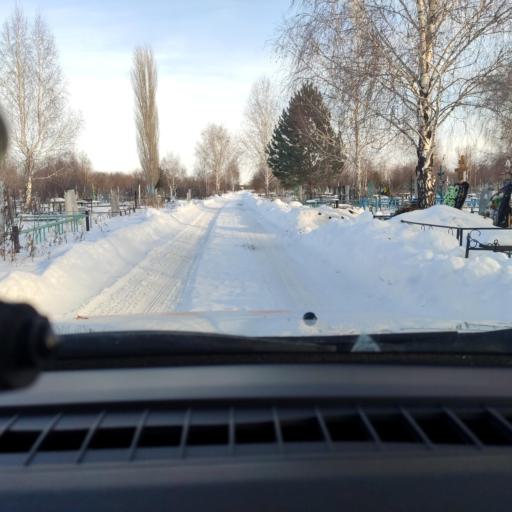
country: RU
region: Samara
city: Chapayevsk
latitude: 52.9893
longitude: 49.7494
